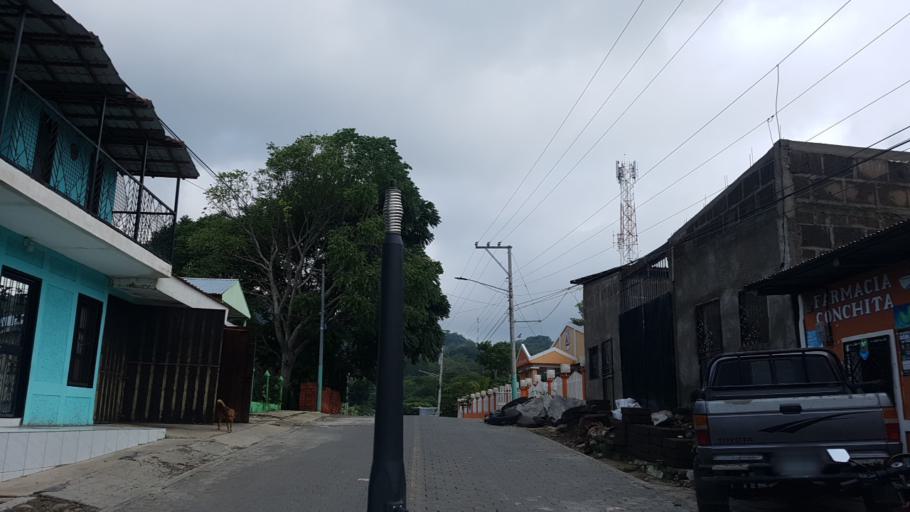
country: NI
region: Leon
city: Santa Rosa del Penon
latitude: 12.9320
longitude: -86.3479
